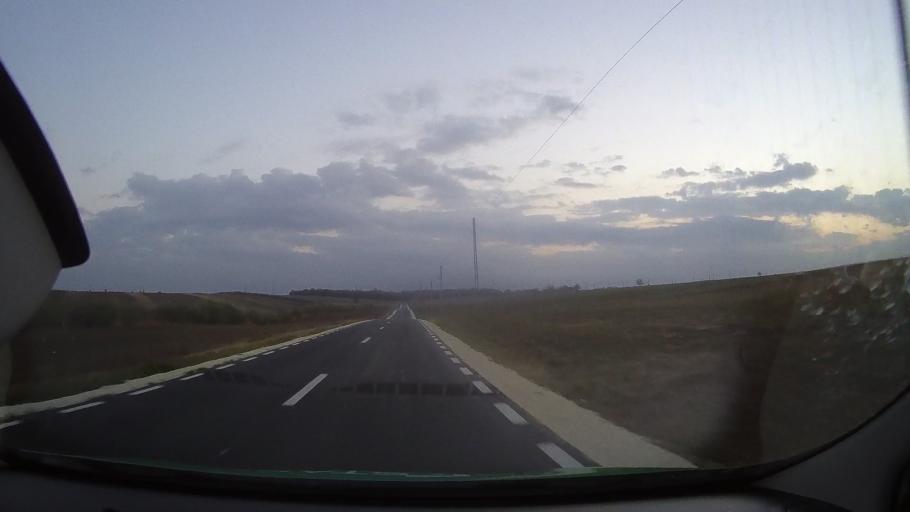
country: RO
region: Constanta
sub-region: Comuna Oltina
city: Oltina
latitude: 44.1200
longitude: 27.6669
